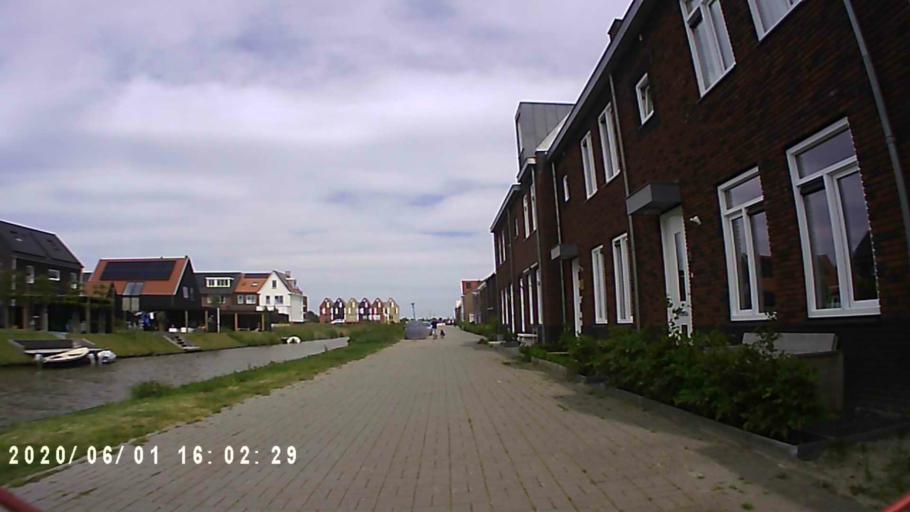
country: NL
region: Friesland
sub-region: Gemeente Leeuwarden
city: Goutum
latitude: 53.1737
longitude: 5.8184
